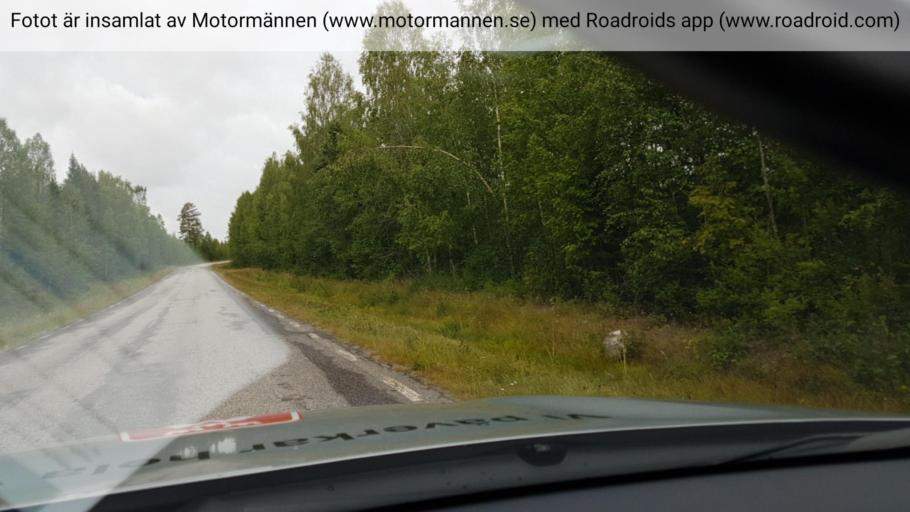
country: SE
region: Norrbotten
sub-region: Bodens Kommun
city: Saevast
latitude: 65.6674
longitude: 21.7267
